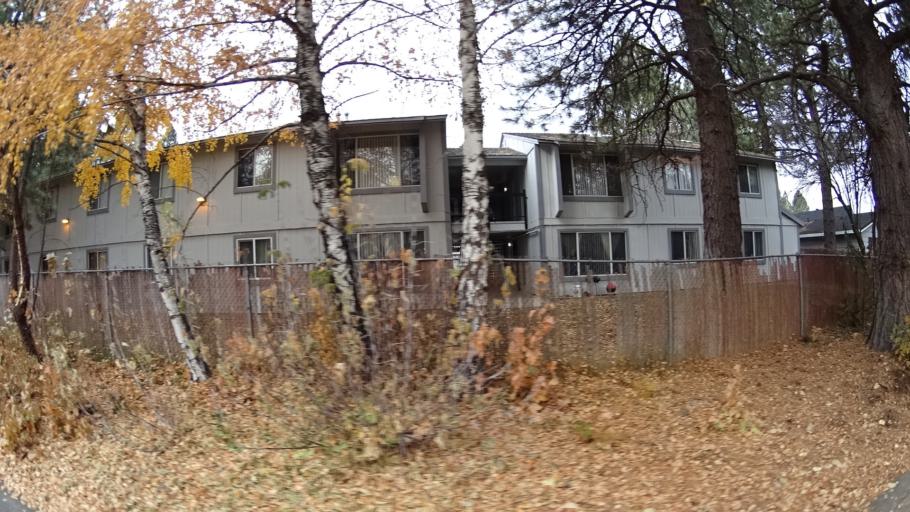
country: US
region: California
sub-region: Siskiyou County
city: Weed
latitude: 41.4135
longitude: -122.3858
